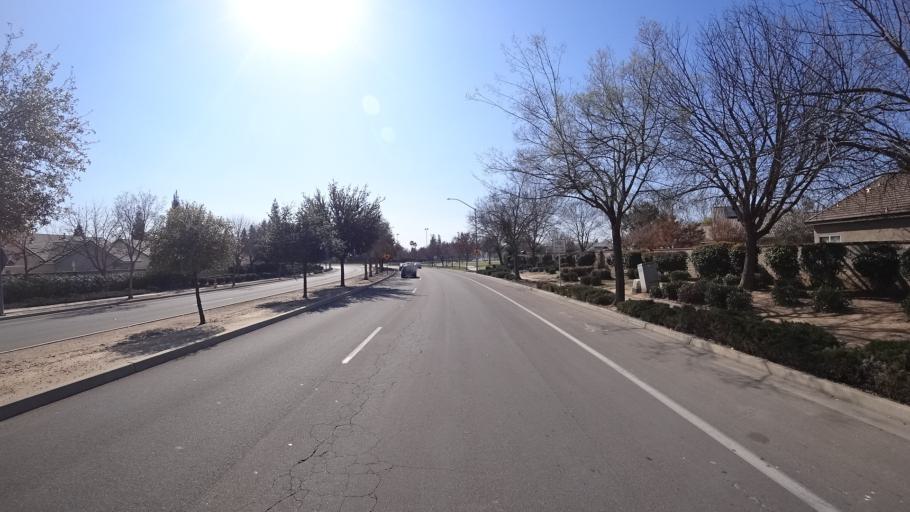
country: US
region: California
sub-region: Fresno County
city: Clovis
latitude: 36.8797
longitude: -119.7477
